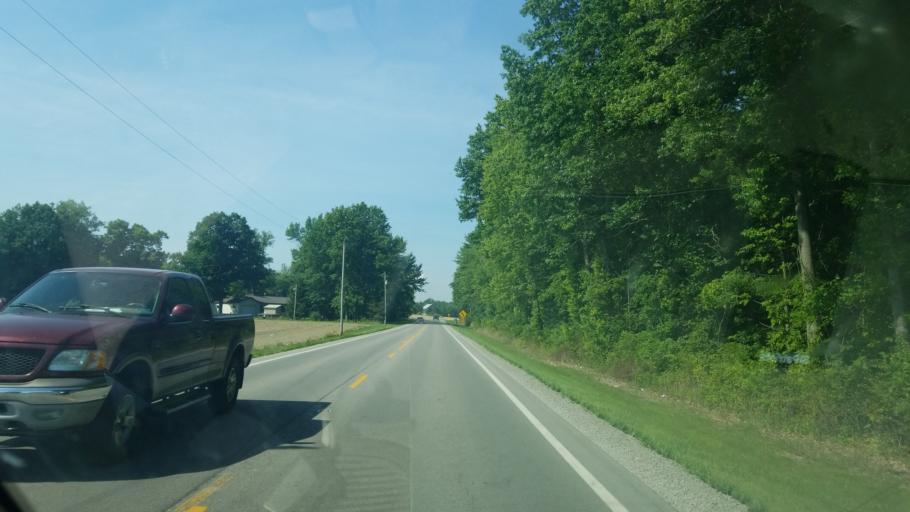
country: US
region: Ohio
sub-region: Wyandot County
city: Carey
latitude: 40.9776
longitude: -83.2699
